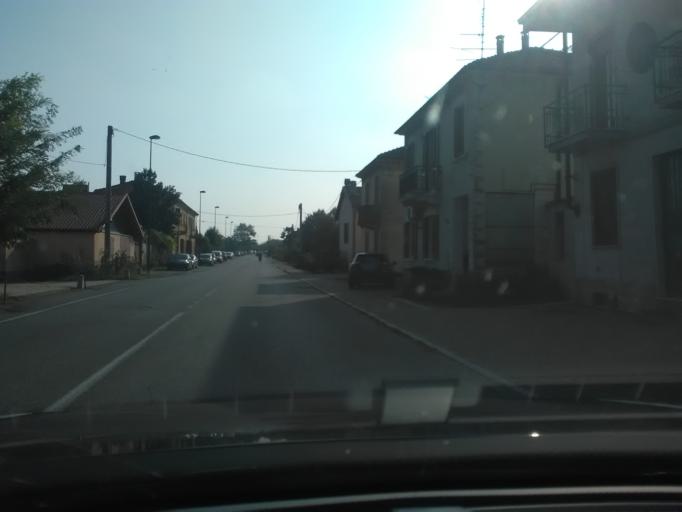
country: IT
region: Piedmont
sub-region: Provincia di Alessandria
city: Casale Monferrato
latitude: 45.1473
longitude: 8.4509
